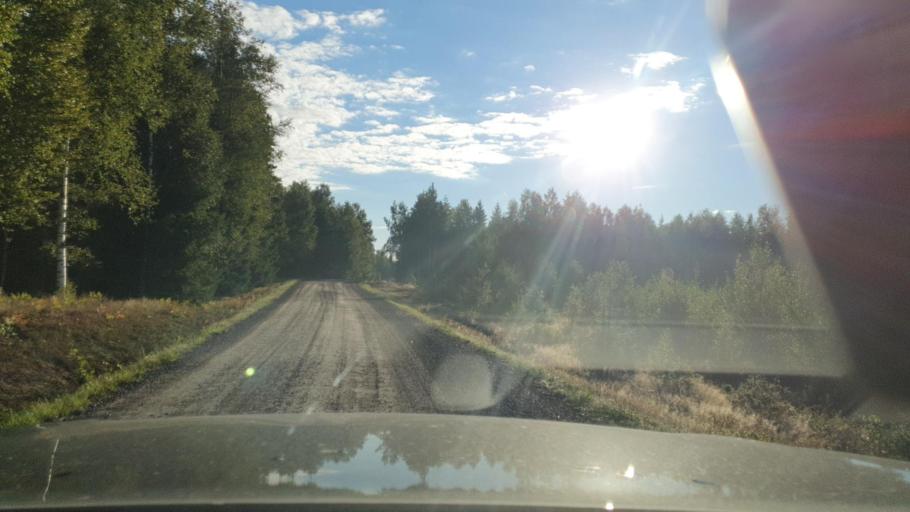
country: SE
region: Vaermland
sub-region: Kristinehamns Kommun
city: Bjorneborg
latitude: 59.1788
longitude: 14.1579
